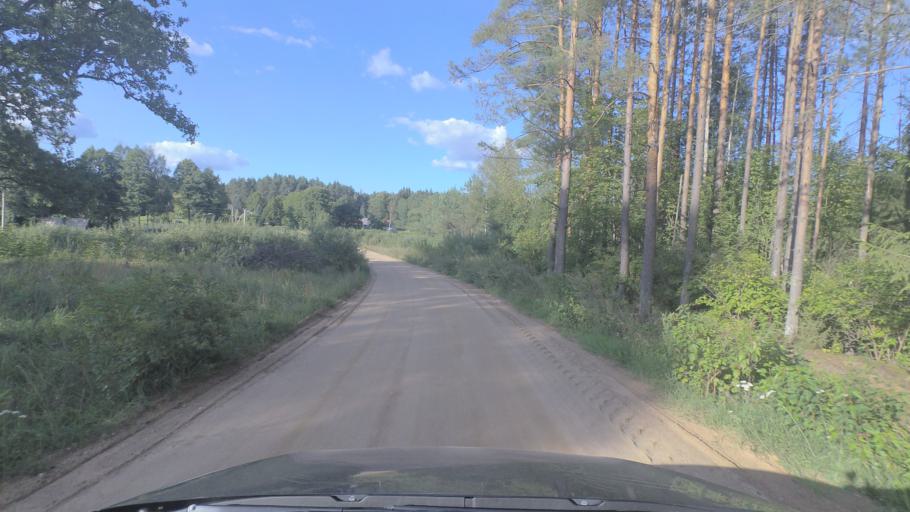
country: LT
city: Pabrade
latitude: 55.1486
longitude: 25.7646
